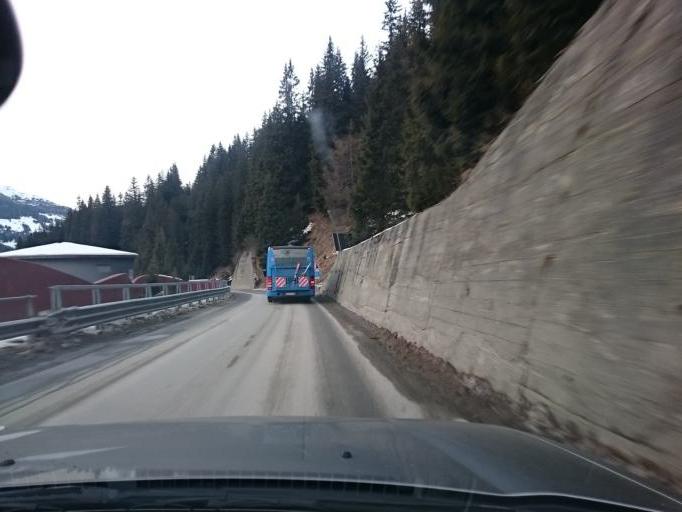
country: IT
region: Lombardy
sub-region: Provincia di Sondrio
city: Sant'Antonio
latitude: 46.4179
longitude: 10.4833
